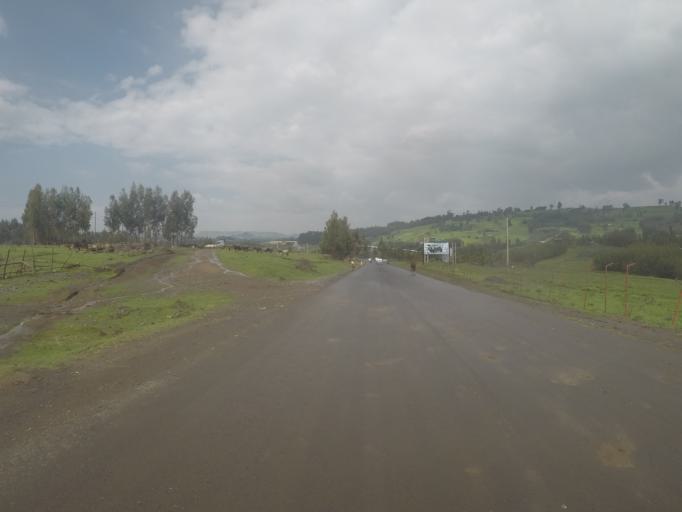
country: ET
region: Amhara
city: Debark'
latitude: 13.1277
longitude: 37.8881
